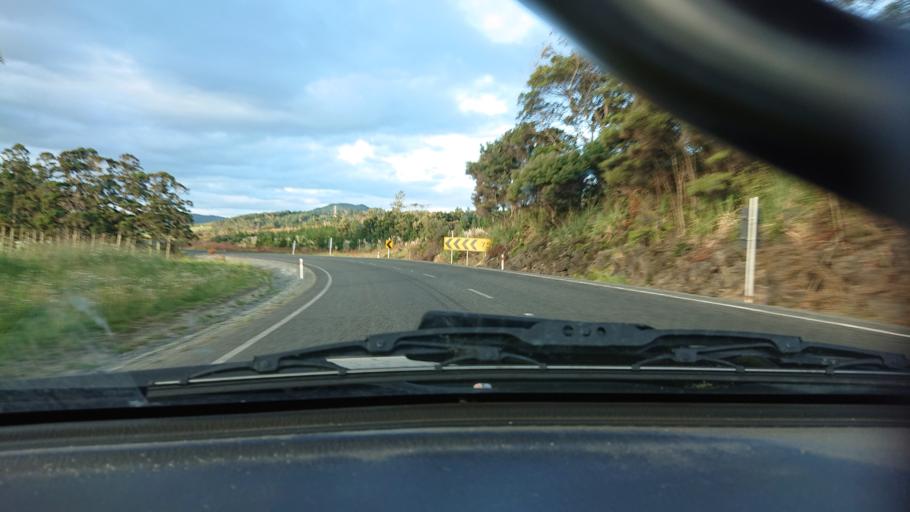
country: NZ
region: Auckland
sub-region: Auckland
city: Parakai
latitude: -36.5139
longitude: 174.4524
